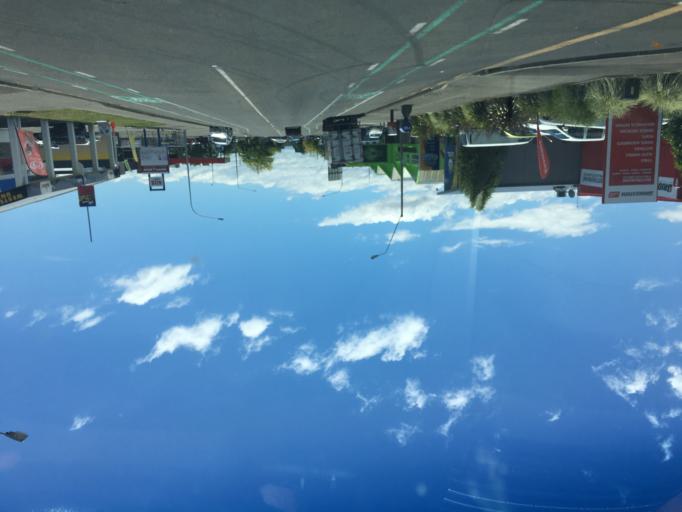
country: NZ
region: Hawke's Bay
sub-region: Hastings District
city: Hastings
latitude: -39.6437
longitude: 176.8505
